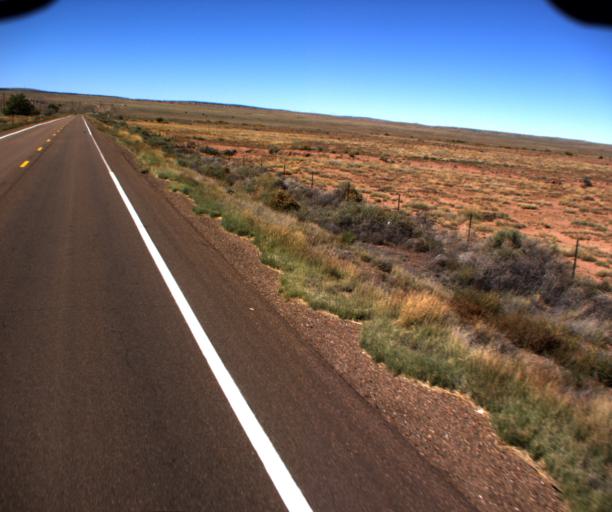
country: US
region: Arizona
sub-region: Apache County
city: Saint Johns
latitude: 34.5078
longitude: -109.4271
